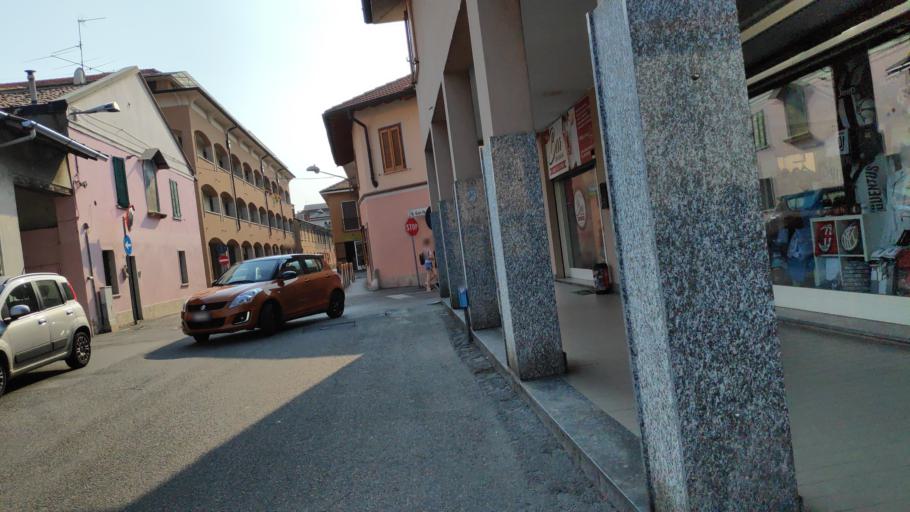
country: IT
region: Lombardy
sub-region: Citta metropolitana di Milano
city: Paullo
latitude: 45.4175
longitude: 9.4022
